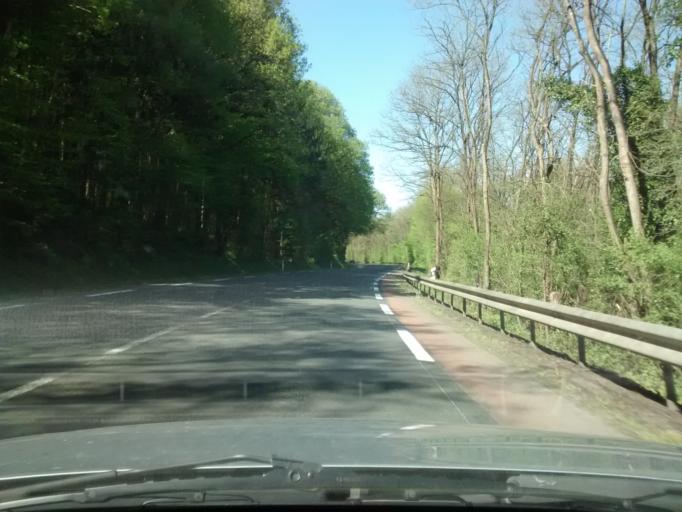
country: FR
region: Pays de la Loire
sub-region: Departement de la Sarthe
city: Brulon
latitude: 48.0265
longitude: -0.2484
